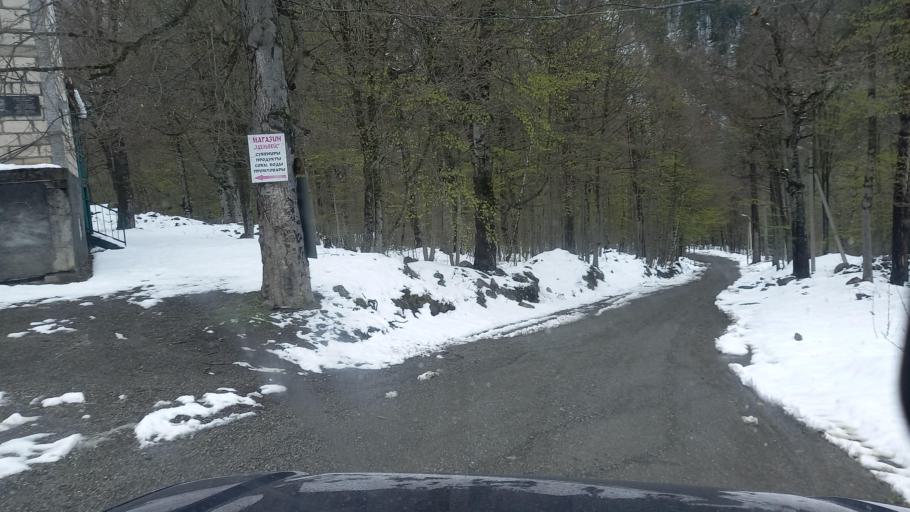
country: RU
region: North Ossetia
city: Mizur
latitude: 42.7868
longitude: 43.9032
